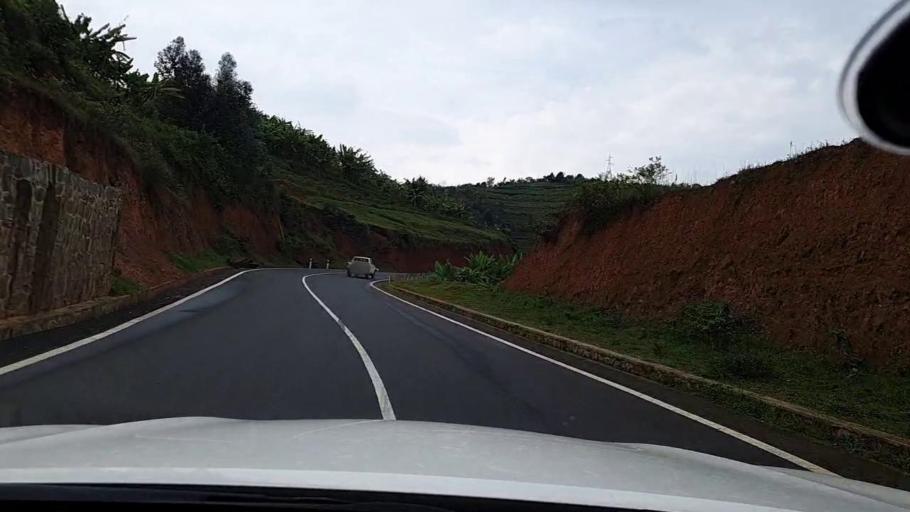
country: RW
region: Western Province
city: Kibuye
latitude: -2.1660
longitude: 29.2922
